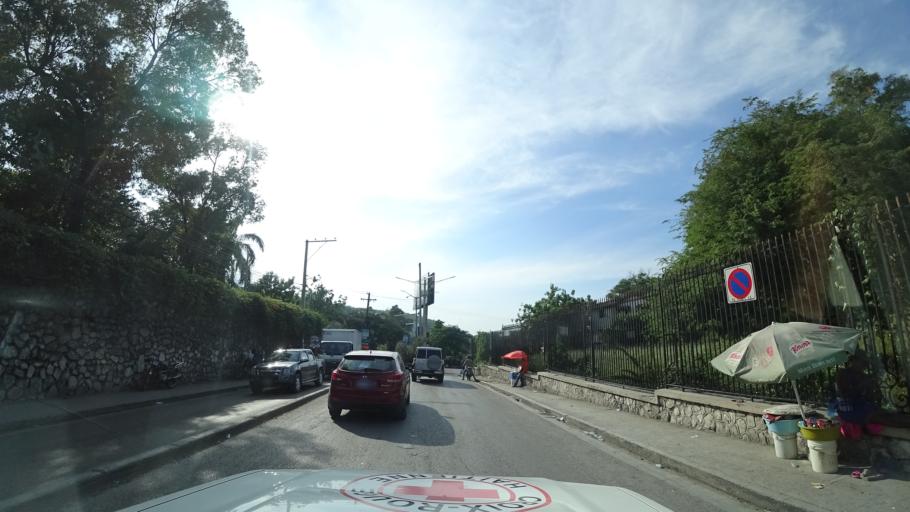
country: HT
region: Ouest
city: Delmas 73
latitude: 18.5306
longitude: -72.3003
